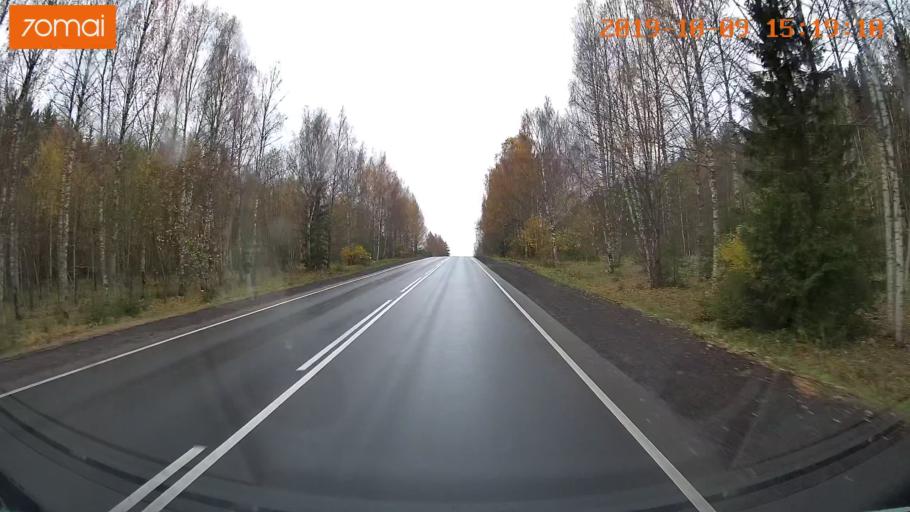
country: RU
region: Kostroma
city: Susanino
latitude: 58.0785
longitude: 41.5610
